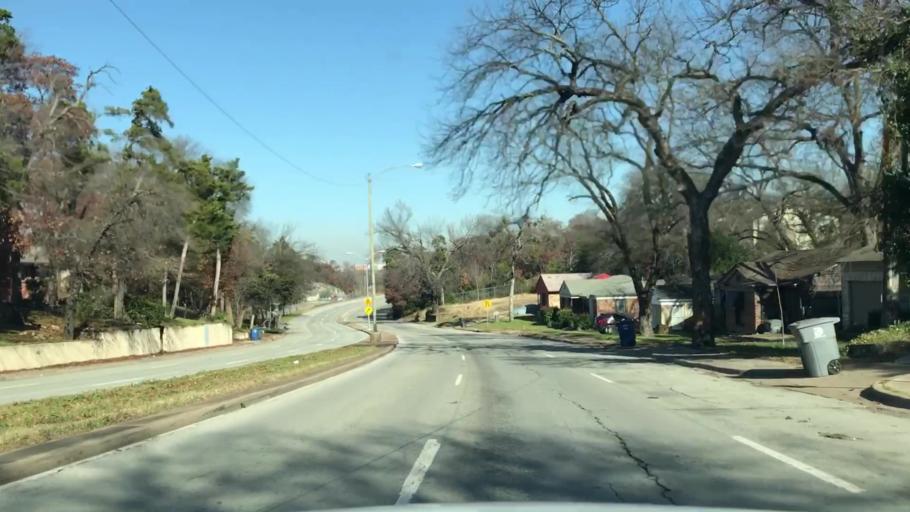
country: US
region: Texas
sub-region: Dallas County
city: Dallas
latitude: 32.7336
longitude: -96.8140
